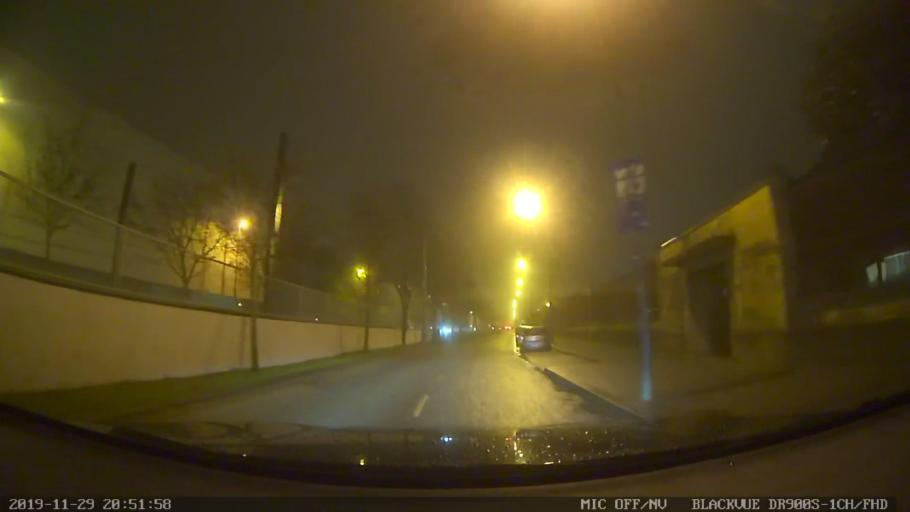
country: PT
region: Porto
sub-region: Matosinhos
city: Senhora da Hora
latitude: 41.1839
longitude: -8.6534
